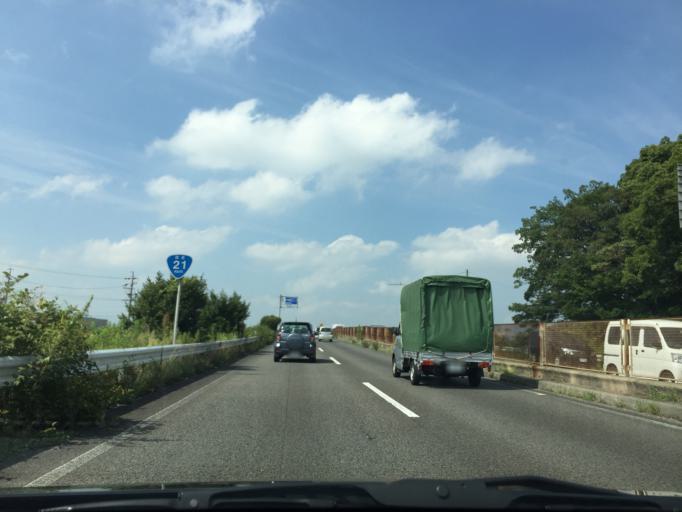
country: JP
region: Gifu
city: Ogaki
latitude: 35.3791
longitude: 136.6676
